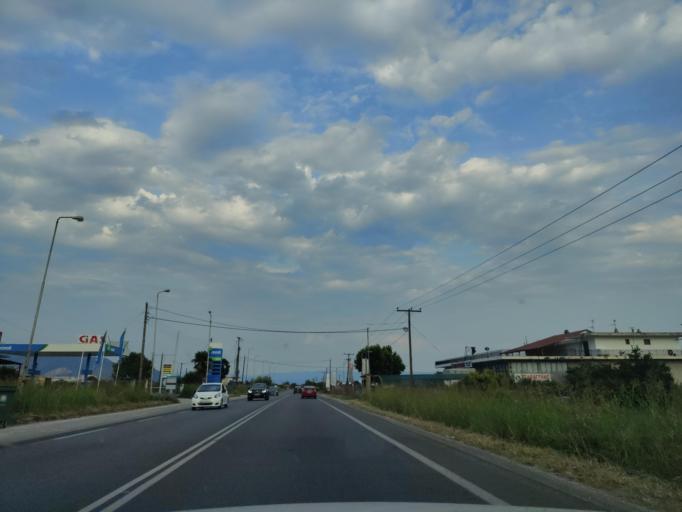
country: GR
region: East Macedonia and Thrace
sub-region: Nomos Dramas
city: Xiropotamos
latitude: 41.1600
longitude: 24.0879
